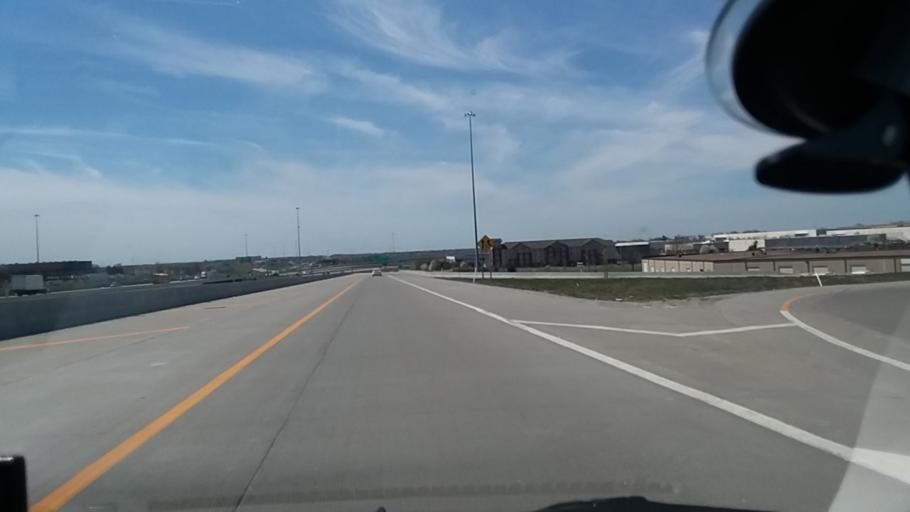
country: US
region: Kansas
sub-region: Johnson County
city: Lenexa
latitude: 38.9431
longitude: -94.7575
